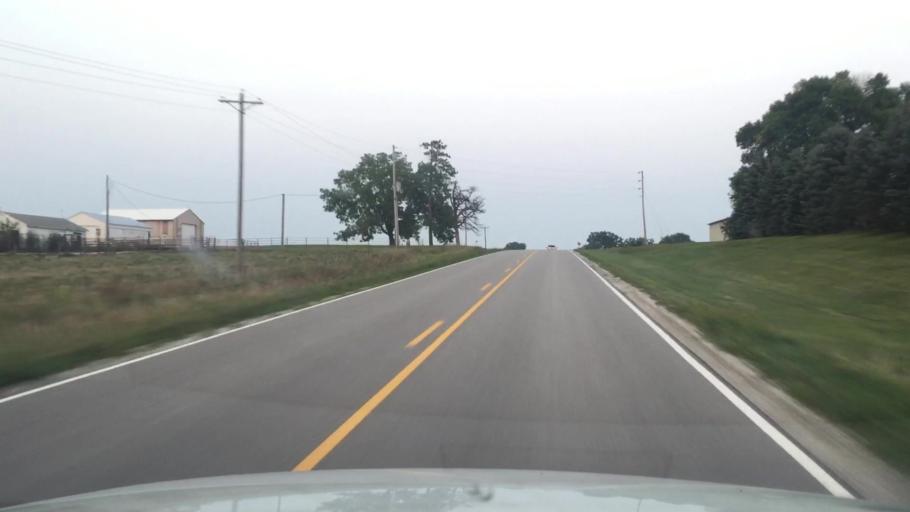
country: US
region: Iowa
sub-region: Warren County
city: Indianola
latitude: 41.1907
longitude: -93.5842
